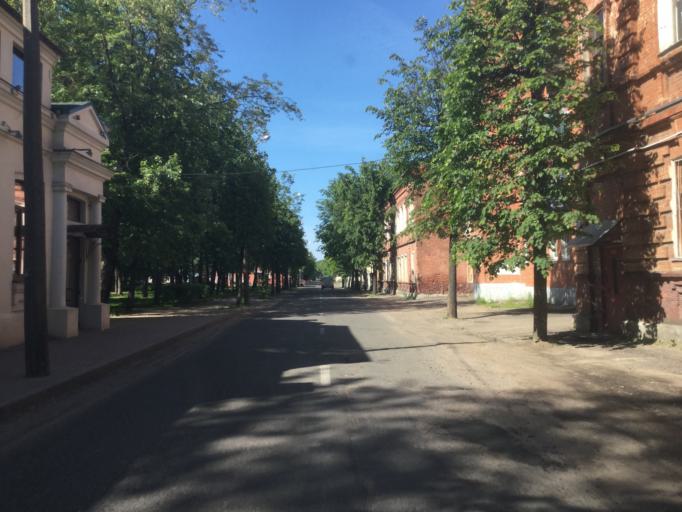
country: BY
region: Vitebsk
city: Vitebsk
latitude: 55.1900
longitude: 30.1909
